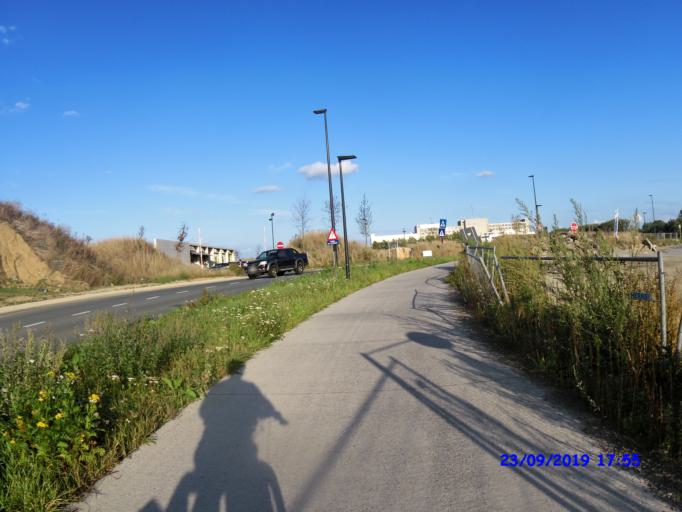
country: BE
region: Flanders
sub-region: Provincie Oost-Vlaanderen
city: Aalst
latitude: 50.9352
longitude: 4.0118
